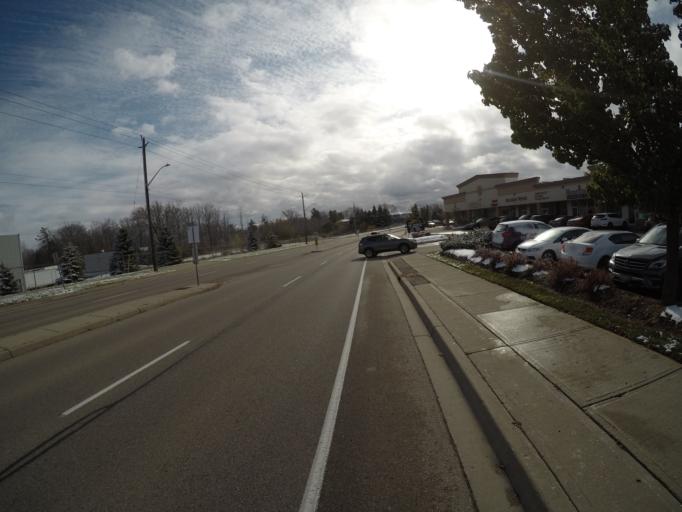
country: CA
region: Ontario
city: Waterloo
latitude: 43.4952
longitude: -80.4904
